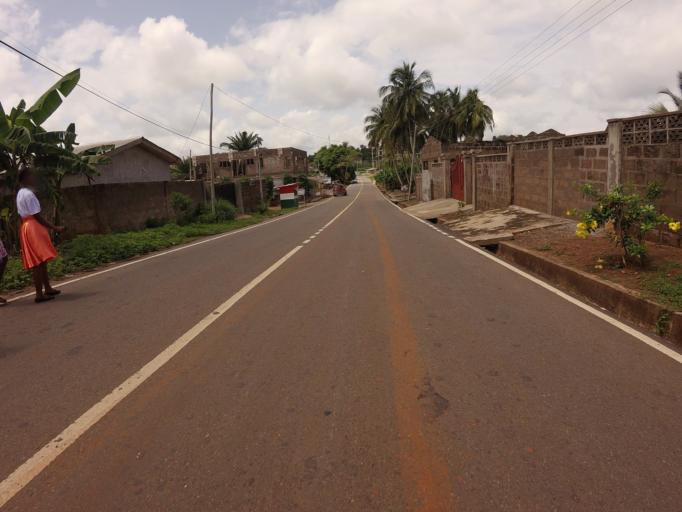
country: GH
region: Volta
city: Ho
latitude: 6.6112
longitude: 0.4572
